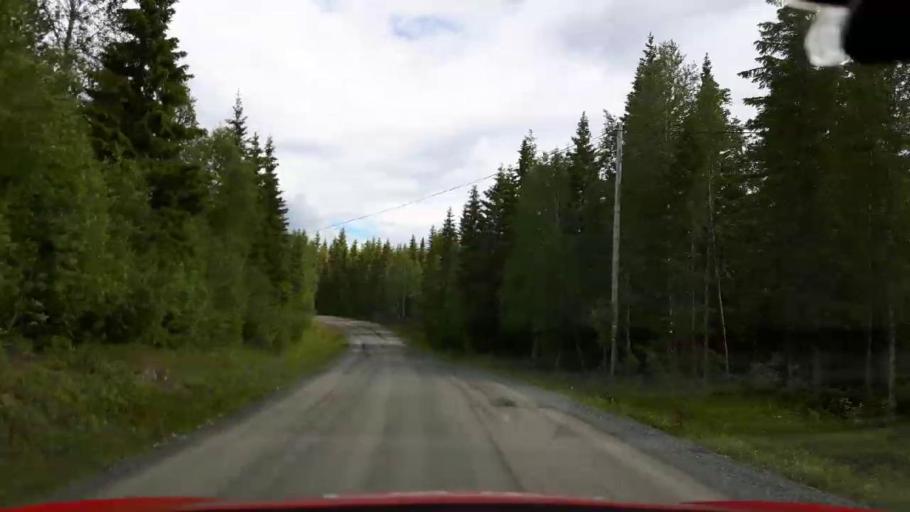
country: NO
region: Nord-Trondelag
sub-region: Lierne
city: Sandvika
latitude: 64.1452
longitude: 13.9028
